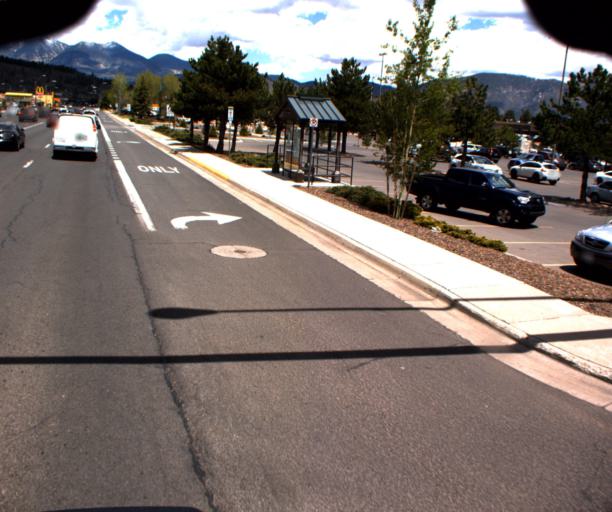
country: US
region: Arizona
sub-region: Coconino County
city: Flagstaff
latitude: 35.1834
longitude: -111.6613
